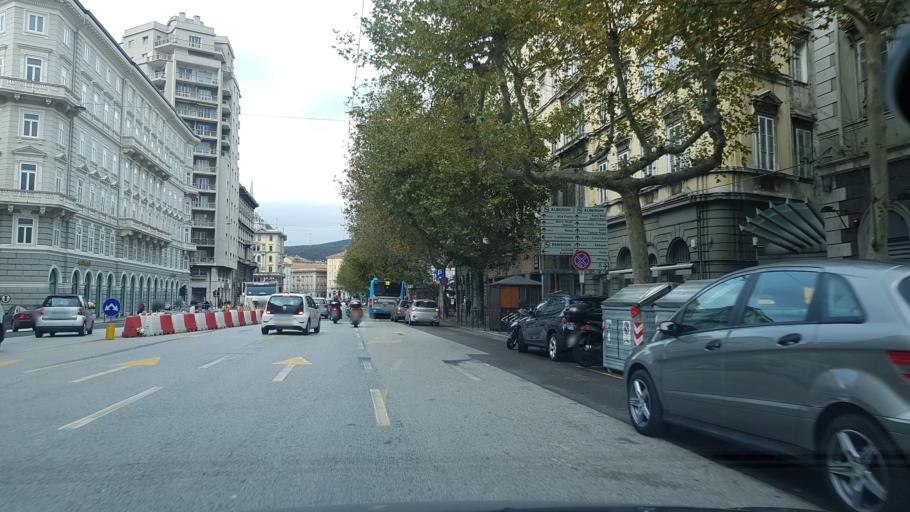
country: IT
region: Friuli Venezia Giulia
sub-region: Provincia di Trieste
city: Trieste
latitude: 45.6523
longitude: 13.7768
